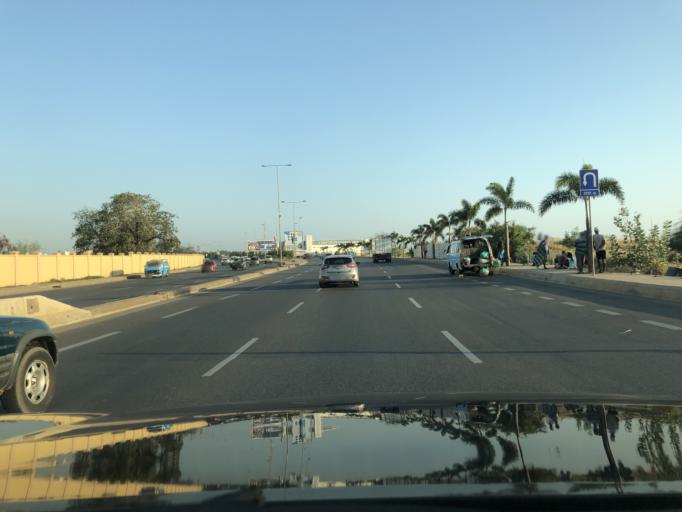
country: AO
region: Luanda
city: Luanda
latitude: -8.9217
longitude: 13.1596
